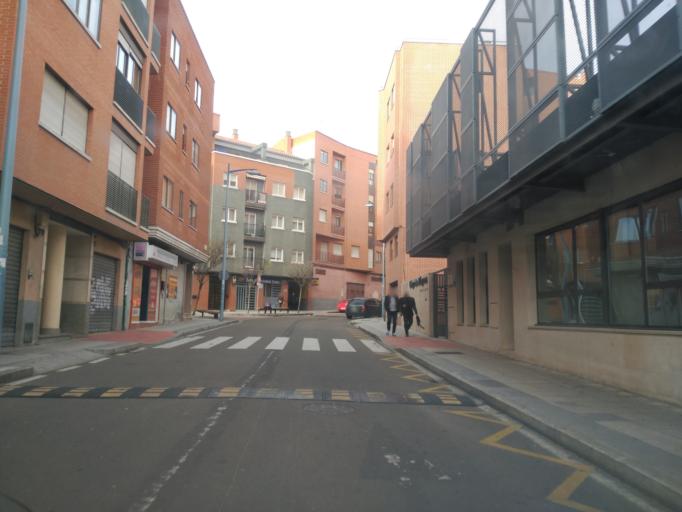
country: ES
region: Castille and Leon
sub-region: Provincia de Salamanca
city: Salamanca
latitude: 40.9620
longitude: -5.6534
